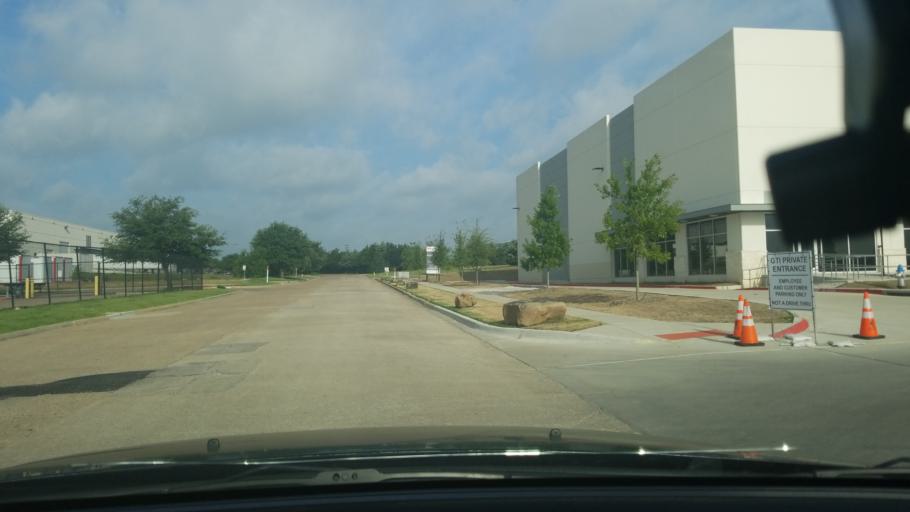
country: US
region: Texas
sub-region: Dallas County
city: Mesquite
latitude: 32.7749
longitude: -96.6484
